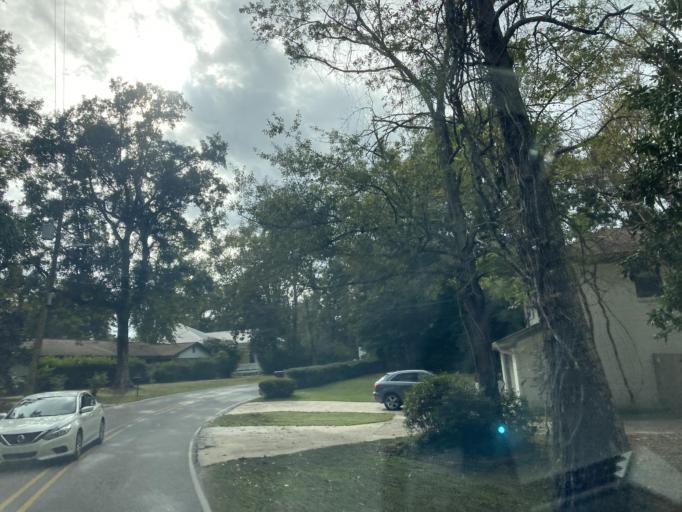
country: US
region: Mississippi
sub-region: Jackson County
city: Gulf Hills
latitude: 30.4297
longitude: -88.8313
